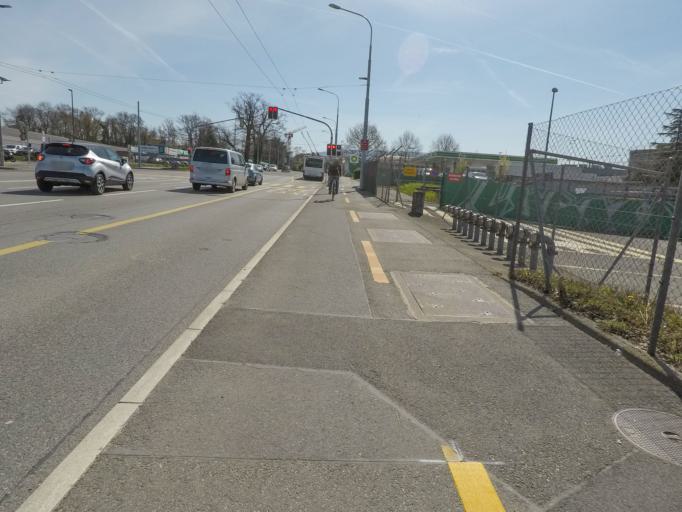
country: CH
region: Geneva
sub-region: Geneva
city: Les Avanchets
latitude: 46.2139
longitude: 6.1026
